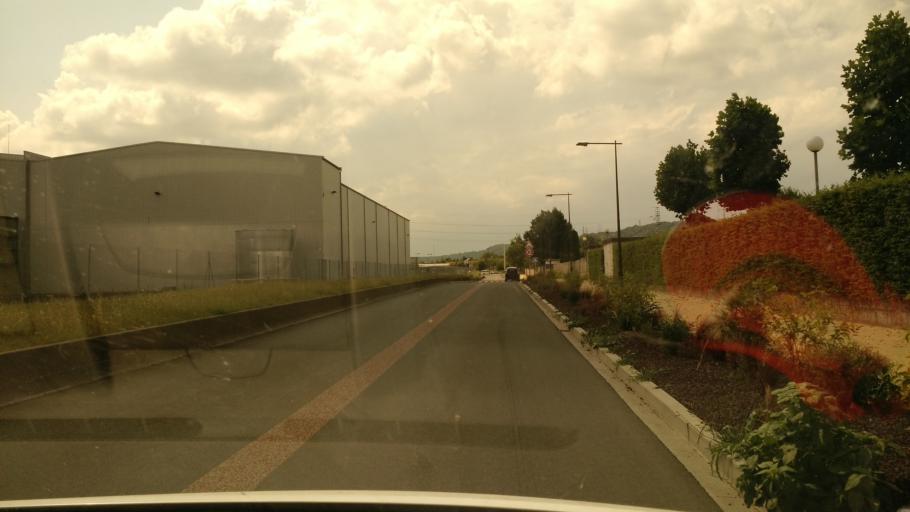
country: FR
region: Rhone-Alpes
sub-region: Departement de l'Ain
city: Montluel
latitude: 45.8424
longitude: 5.0533
